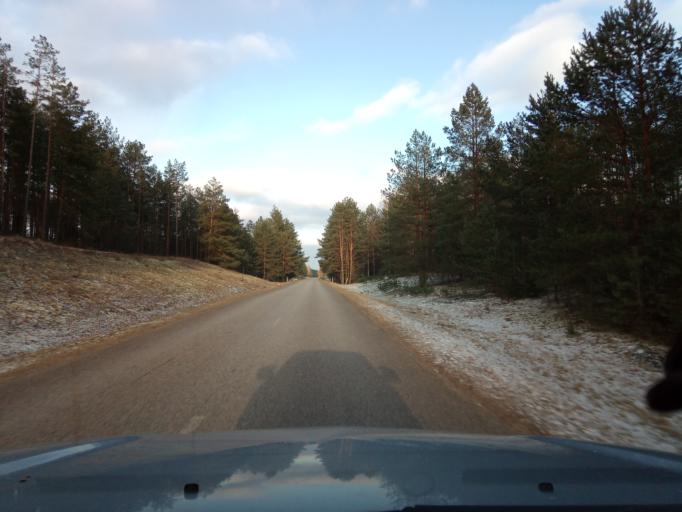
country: LT
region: Alytaus apskritis
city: Varena
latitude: 54.1156
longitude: 24.4449
